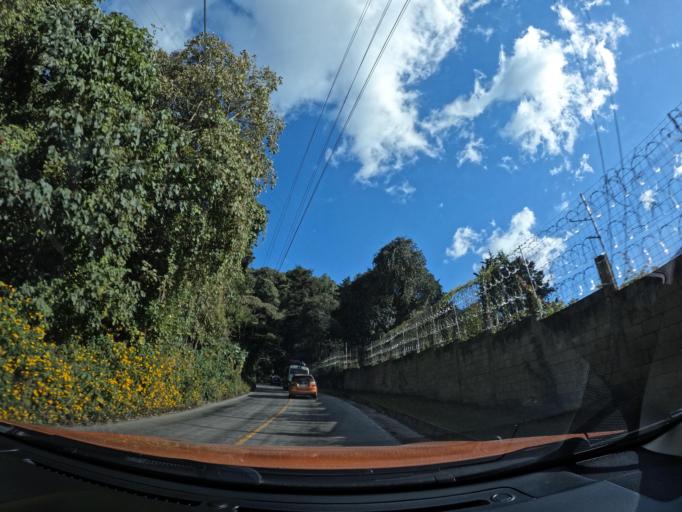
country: GT
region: Sacatepequez
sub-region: Municipio de Santa Maria de Jesus
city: Santa Maria de Jesus
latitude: 14.5061
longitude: -90.7151
